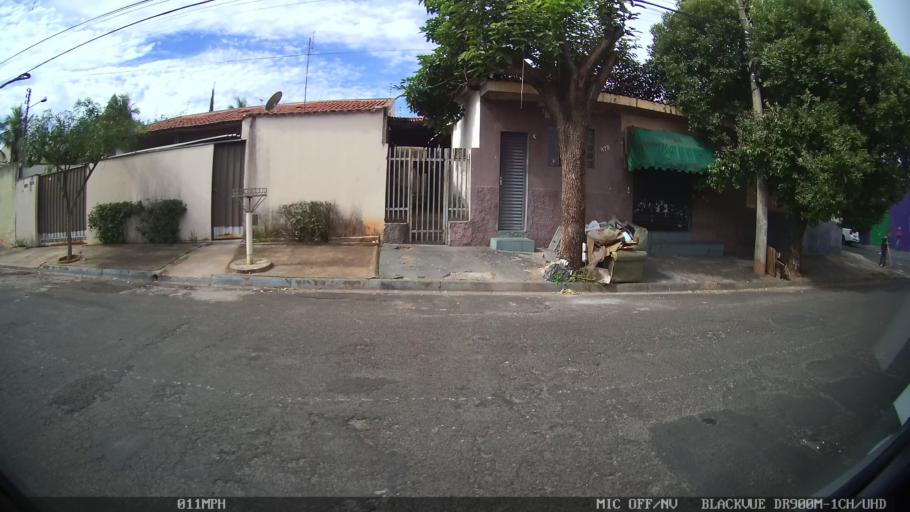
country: BR
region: Sao Paulo
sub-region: Catanduva
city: Catanduva
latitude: -21.1515
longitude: -48.9732
